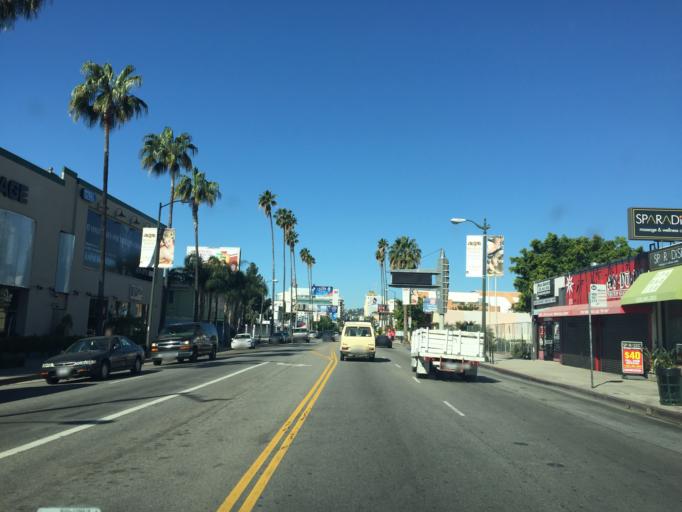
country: US
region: California
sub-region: Los Angeles County
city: Hollywood
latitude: 34.1017
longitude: -118.3181
